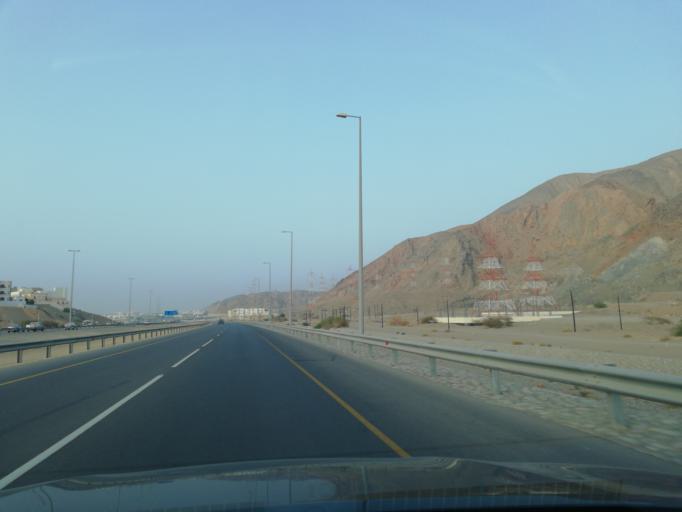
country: OM
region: Muhafazat Masqat
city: Bawshar
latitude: 23.5735
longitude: 58.4313
